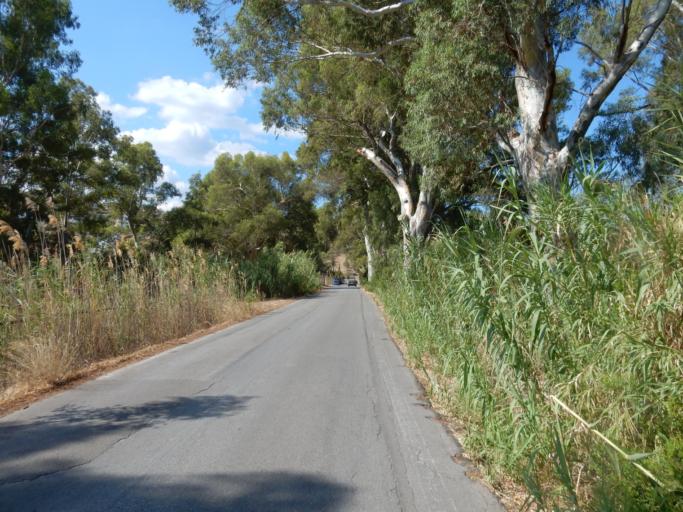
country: GR
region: Attica
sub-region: Nomos Piraios
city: Kypseli
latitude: 37.6989
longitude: 23.4688
